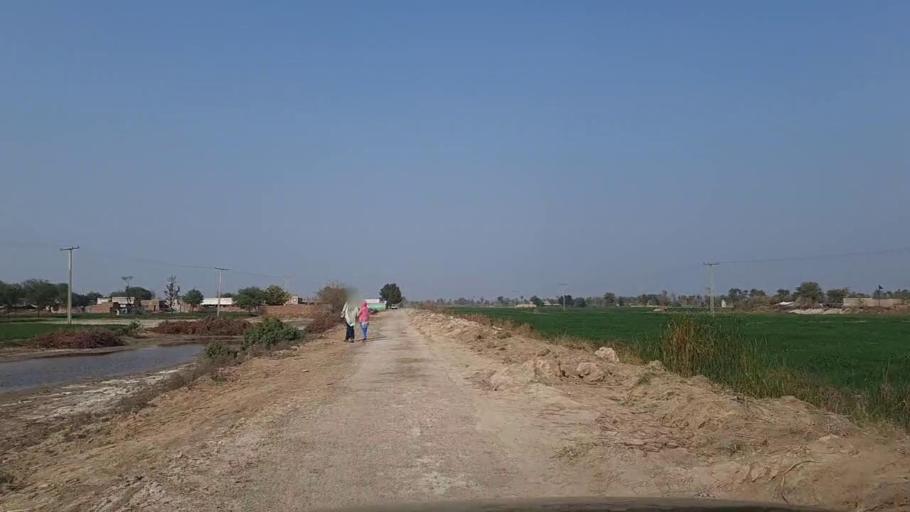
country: PK
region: Sindh
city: Daur
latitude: 26.4087
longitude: 68.4189
